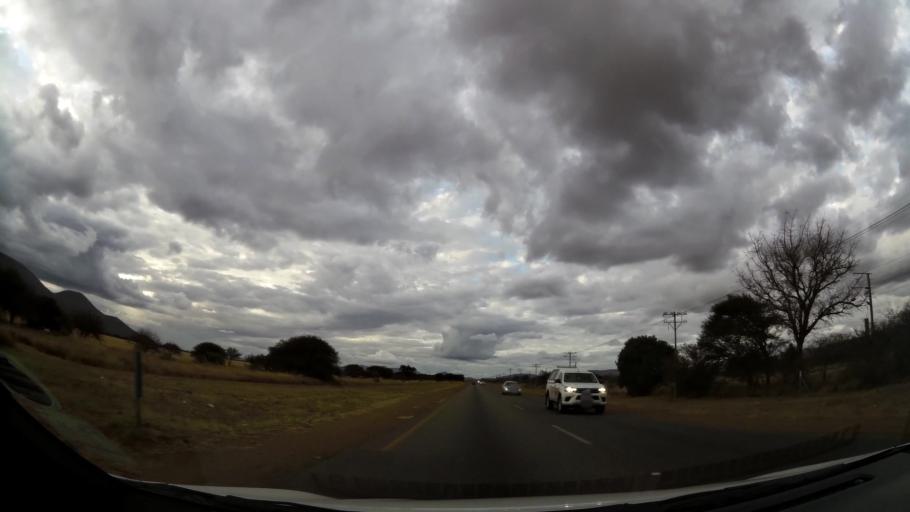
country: ZA
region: Limpopo
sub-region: Waterberg District Municipality
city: Mokopane
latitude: -24.2563
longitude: 28.9877
